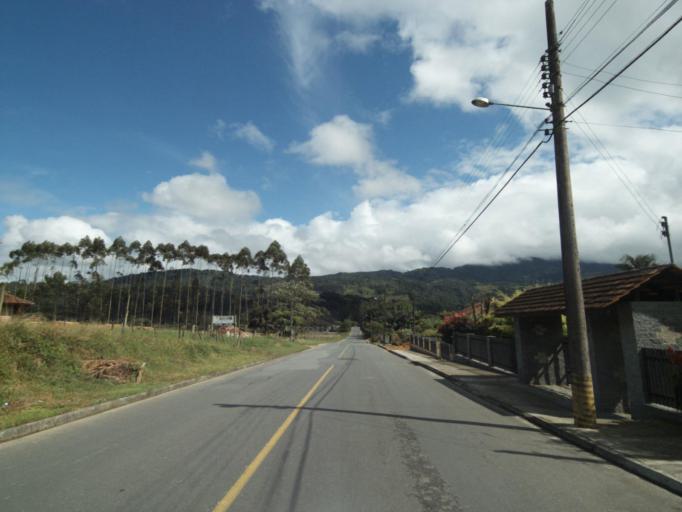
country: BR
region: Santa Catarina
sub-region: Pomerode
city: Pomerode
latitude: -26.6878
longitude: -49.1680
